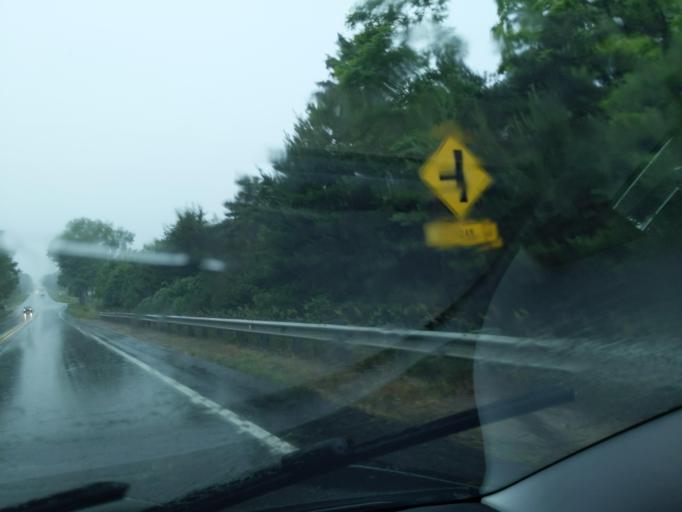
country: US
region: Michigan
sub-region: Muskegon County
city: Fruitport
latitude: 43.1540
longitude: -86.1834
